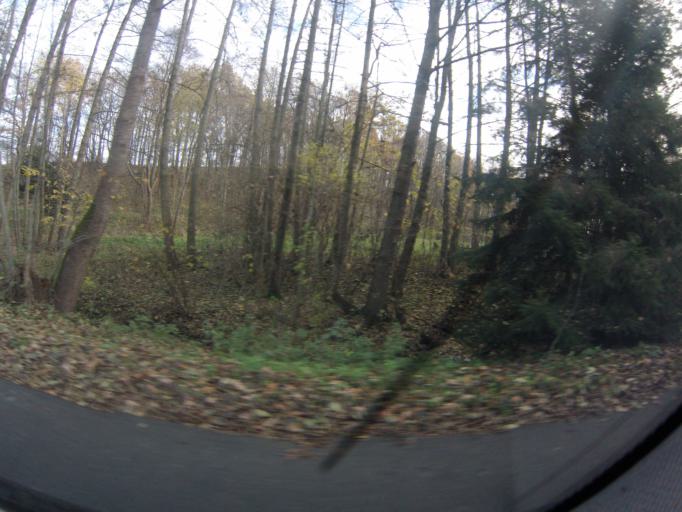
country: DE
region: Thuringia
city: Heyersdorf
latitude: 50.8501
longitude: 12.3592
